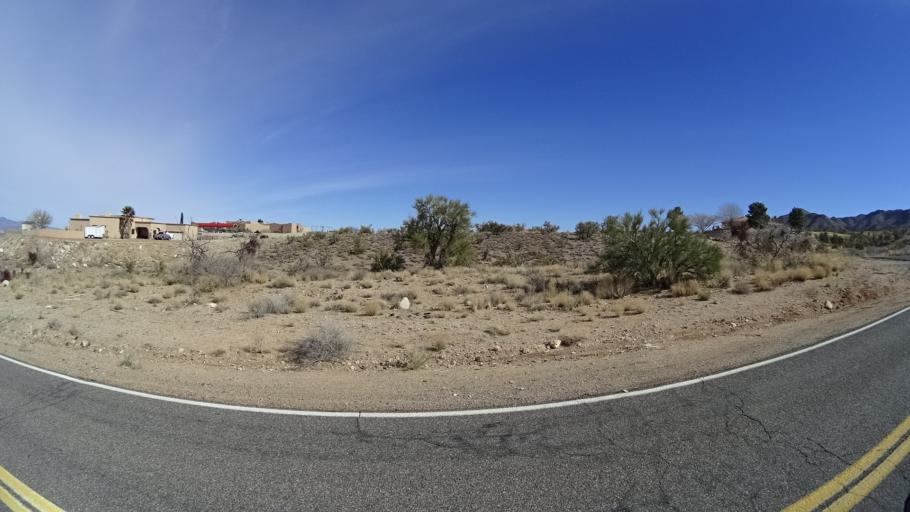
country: US
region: Arizona
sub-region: Mohave County
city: Kingman
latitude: 35.1704
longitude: -113.9799
